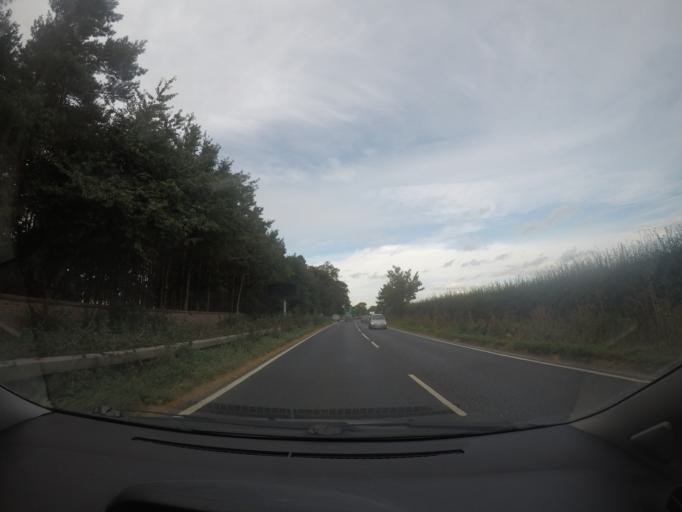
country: GB
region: England
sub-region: City of York
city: Fulford
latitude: 53.9204
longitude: -1.0629
